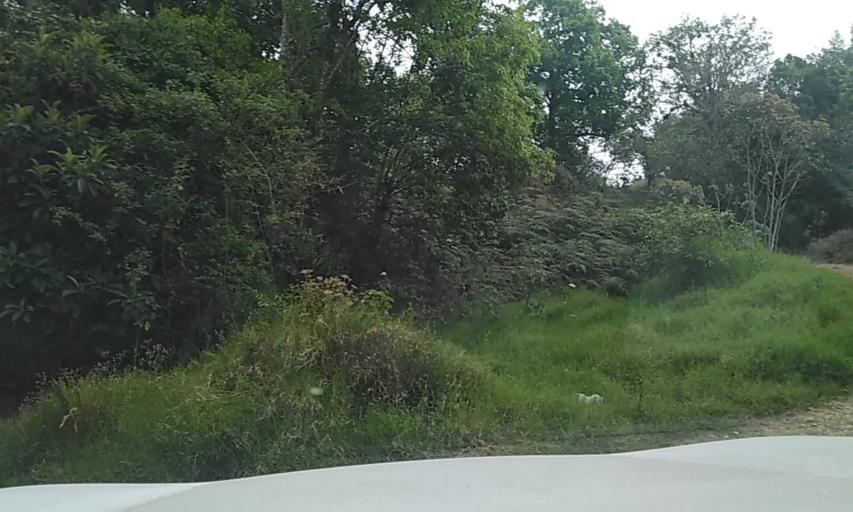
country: MX
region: Veracruz
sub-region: Xalapa
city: Lomas Verdes
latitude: 19.4996
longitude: -96.9170
